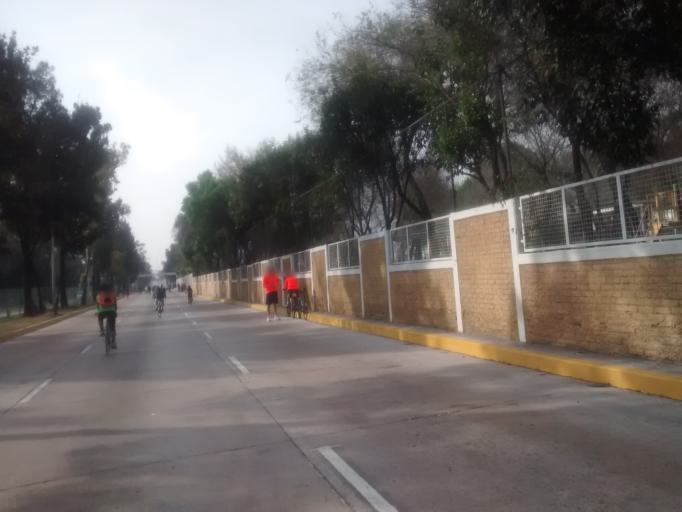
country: MX
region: Mexico City
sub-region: Iztacalco
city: Iztacalco
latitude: 19.3920
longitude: -99.0996
